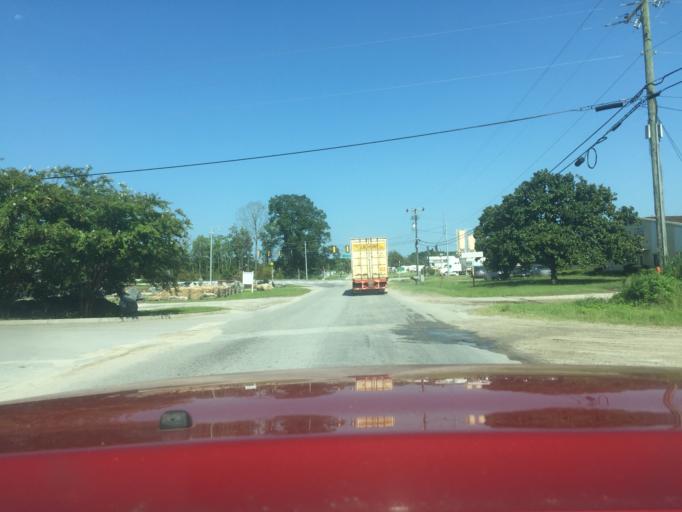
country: US
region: Georgia
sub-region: Chatham County
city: Garden City
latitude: 32.0793
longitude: -81.1559
